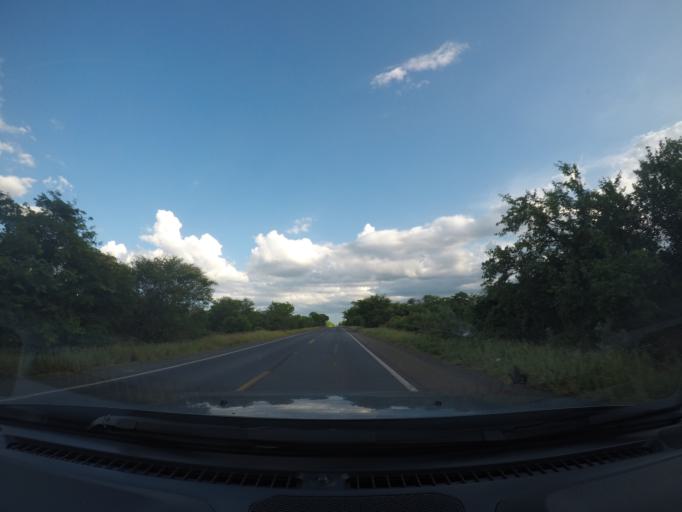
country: BR
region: Bahia
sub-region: Oliveira Dos Brejinhos
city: Beira Rio
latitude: -12.2200
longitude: -42.7926
